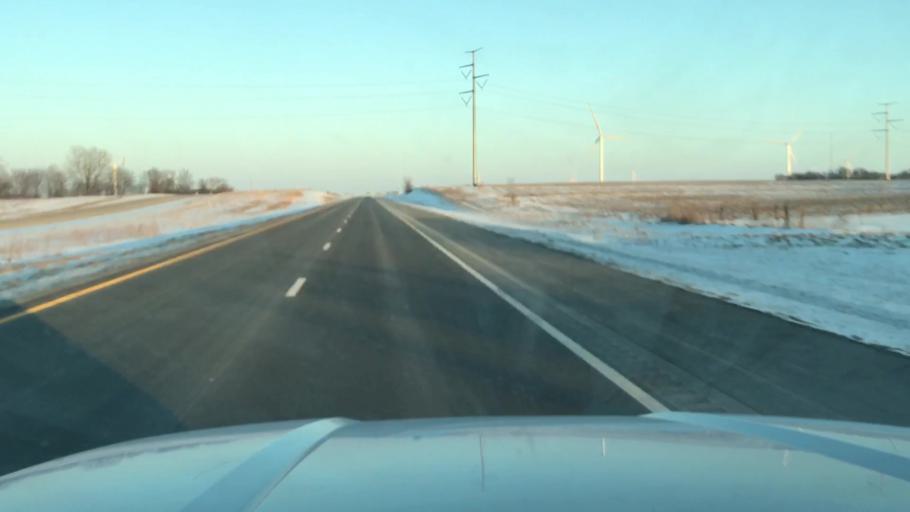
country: US
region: Missouri
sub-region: DeKalb County
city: Maysville
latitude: 39.7618
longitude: -94.4465
